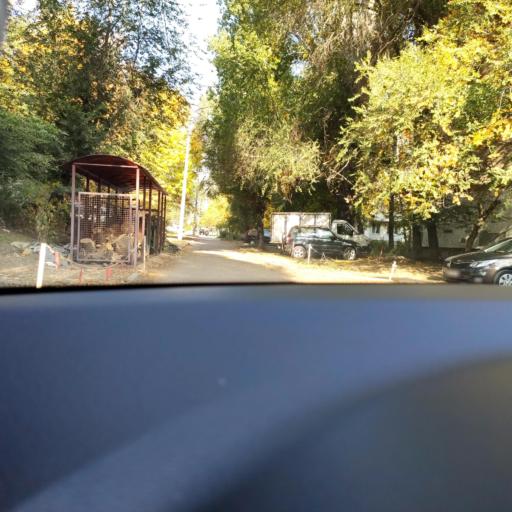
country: RU
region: Samara
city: Petra-Dubrava
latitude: 53.2441
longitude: 50.2622
